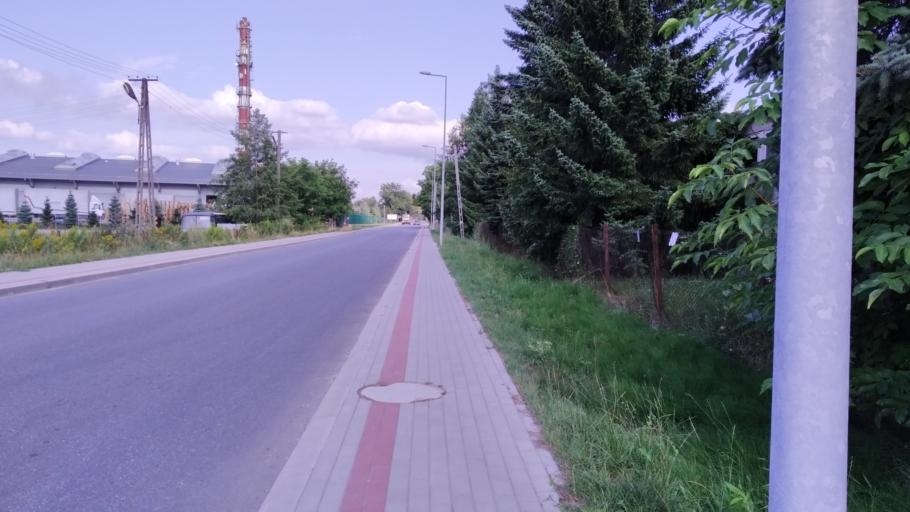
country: PL
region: Subcarpathian Voivodeship
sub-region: Powiat lancucki
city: Lancut
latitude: 50.0787
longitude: 22.2213
